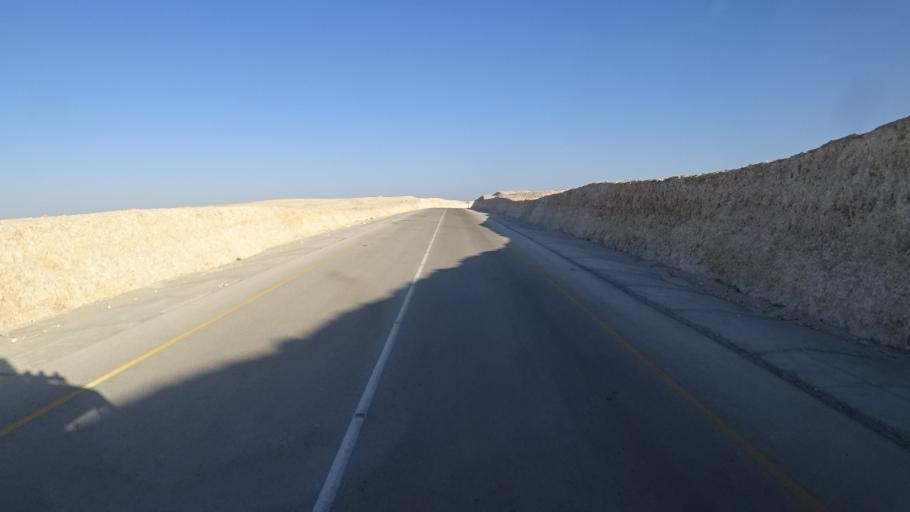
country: YE
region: Al Mahrah
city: Hawf
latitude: 17.0854
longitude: 53.0816
